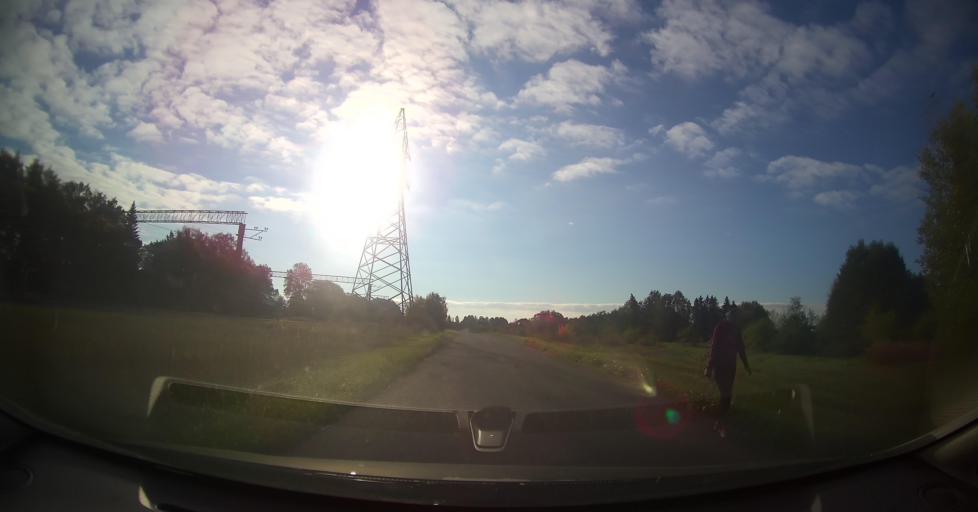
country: EE
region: Harju
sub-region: Joelaehtme vald
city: Loo
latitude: 59.4017
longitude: 24.9253
